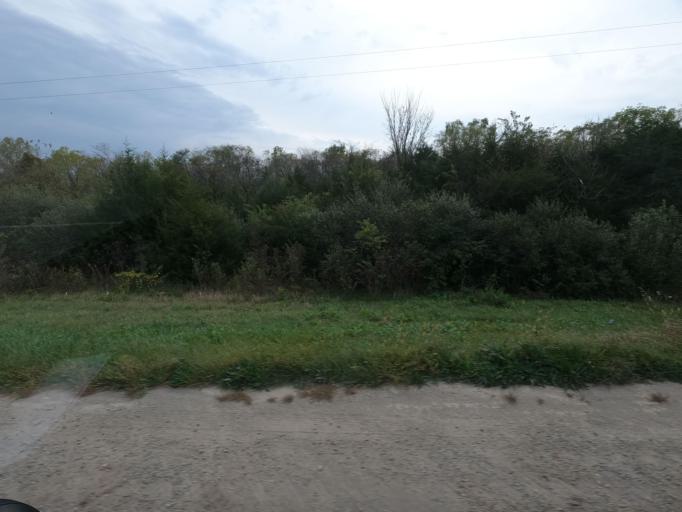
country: US
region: Iowa
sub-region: Van Buren County
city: Keosauqua
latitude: 40.8650
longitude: -92.1407
